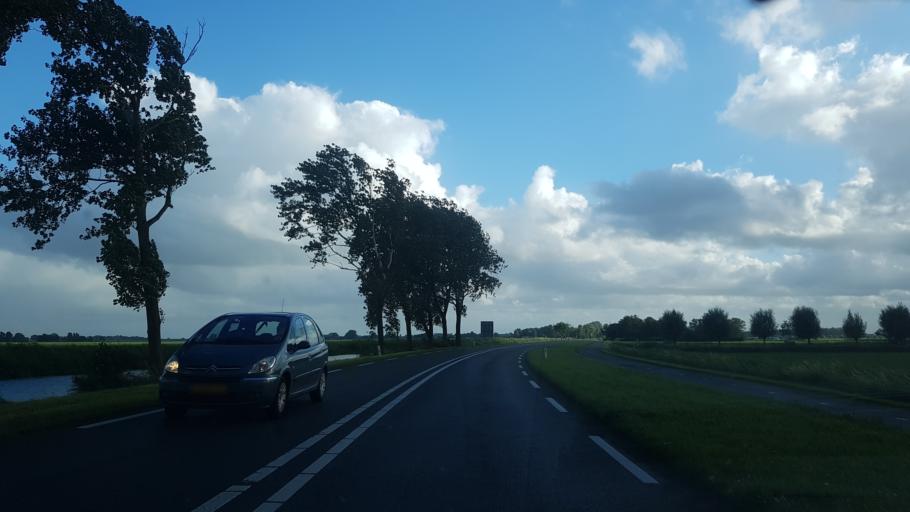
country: NL
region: Groningen
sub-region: Gemeente Slochteren
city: Slochteren
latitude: 53.2917
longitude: 6.7231
